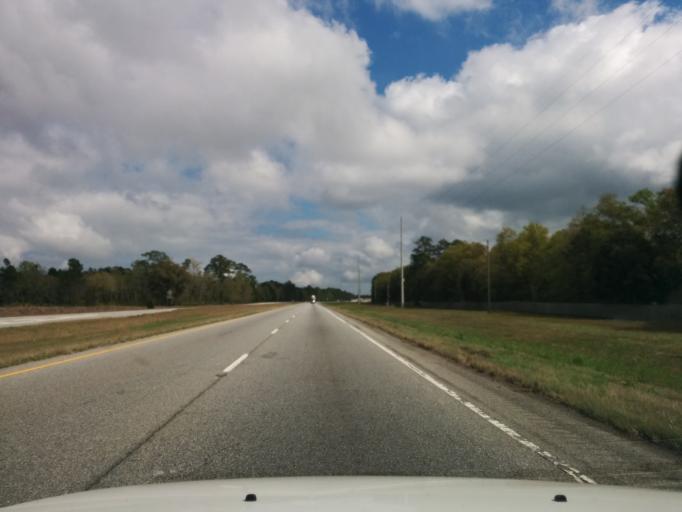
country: US
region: Georgia
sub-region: Glynn County
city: Brunswick
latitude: 31.1329
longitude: -81.5635
